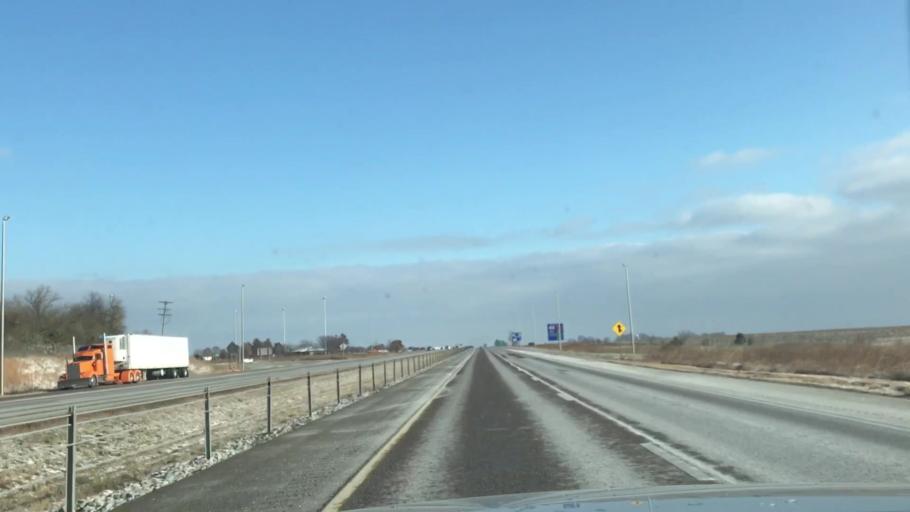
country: US
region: Illinois
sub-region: Madison County
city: Worden
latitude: 38.8679
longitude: -89.8529
